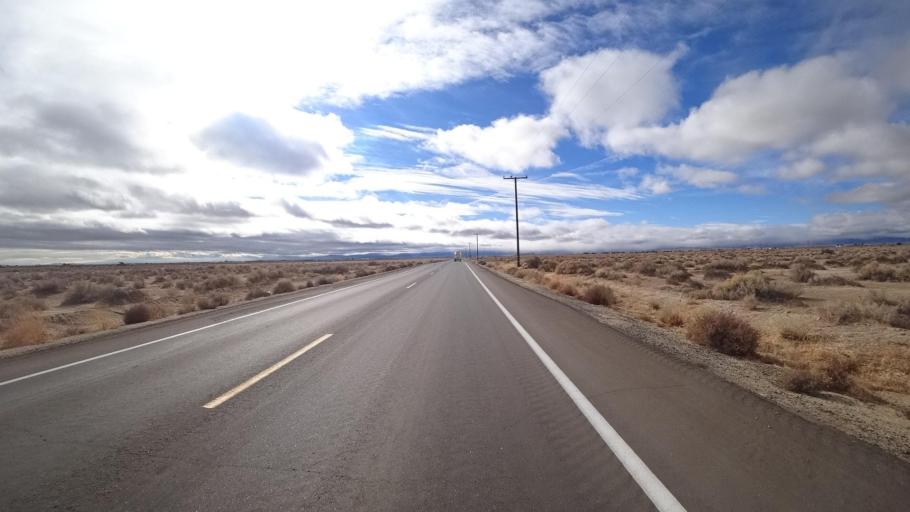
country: US
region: California
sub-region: Kern County
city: Rosamond
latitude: 34.8551
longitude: -118.2909
